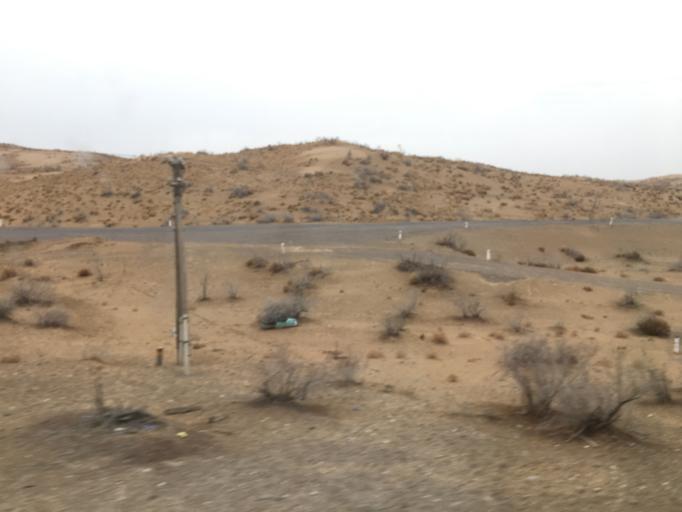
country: TM
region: Mary
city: Yoloeten
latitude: 36.4468
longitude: 62.5880
